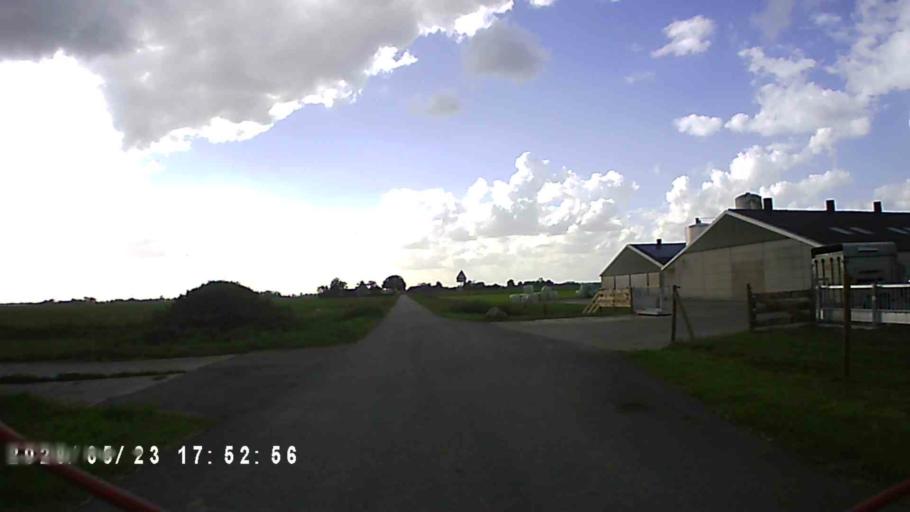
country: NL
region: Groningen
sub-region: Gemeente Slochteren
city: Slochteren
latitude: 53.2434
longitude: 6.7561
